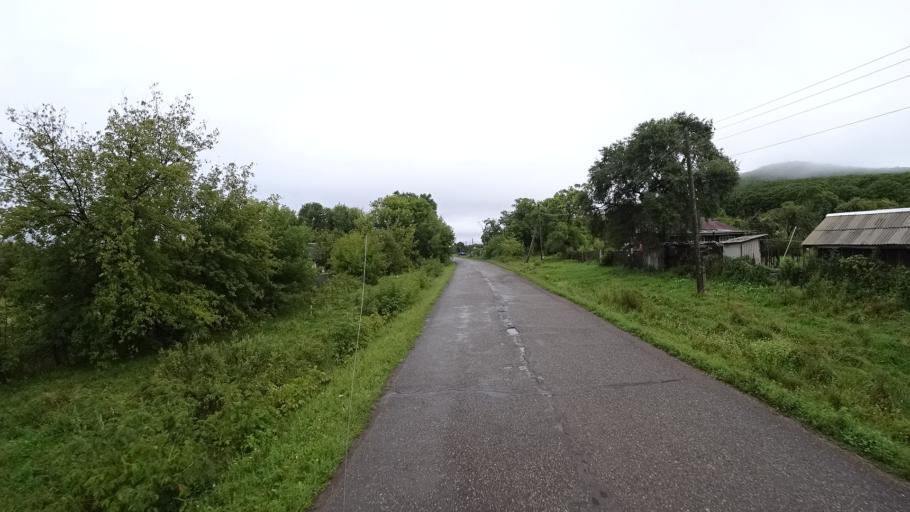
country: RU
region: Primorskiy
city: Monastyrishche
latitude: 44.2686
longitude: 132.4204
